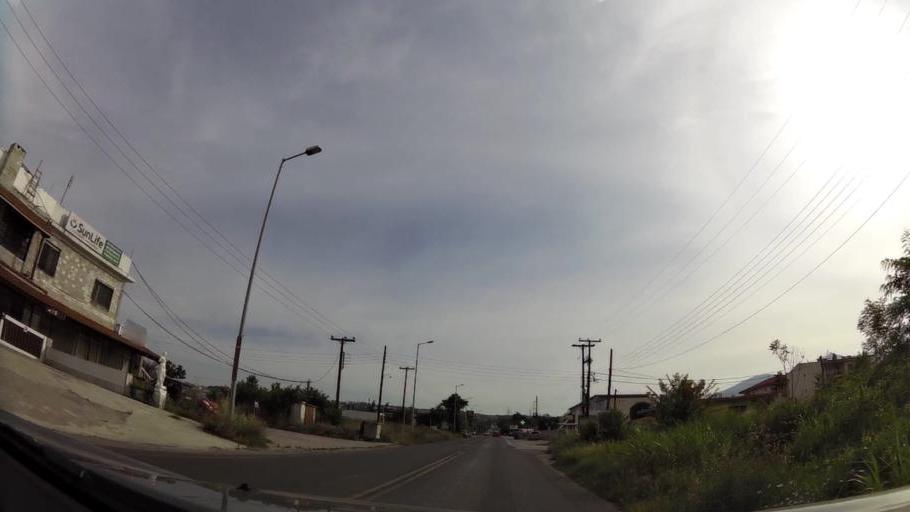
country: GR
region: Central Macedonia
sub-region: Nomos Thessalonikis
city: Thermi
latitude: 40.5576
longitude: 23.0204
